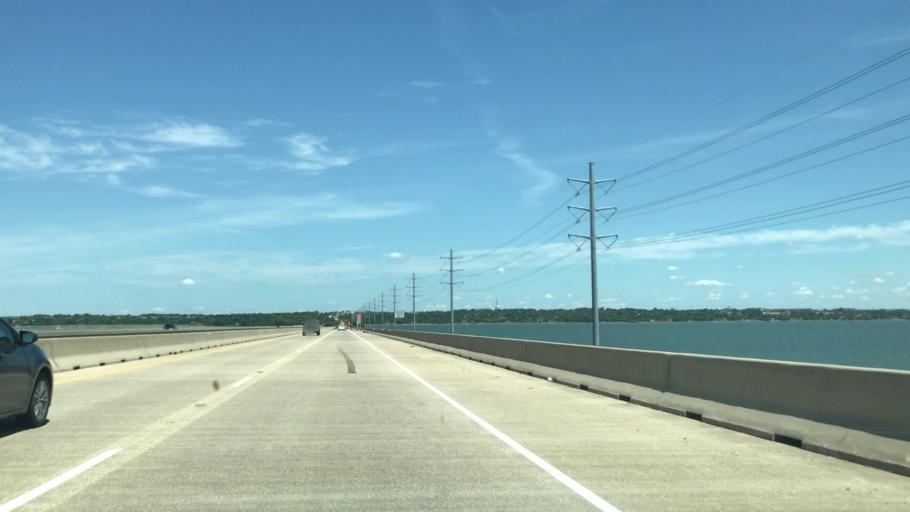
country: US
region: Texas
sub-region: Rockwall County
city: Rockwall
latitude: 32.9220
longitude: -96.5041
